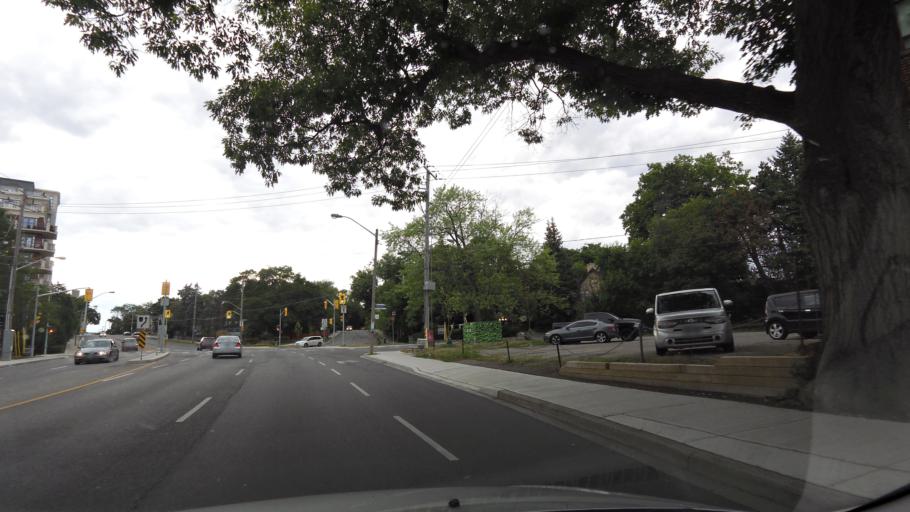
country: CA
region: Ontario
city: Etobicoke
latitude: 43.6501
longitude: -79.4985
